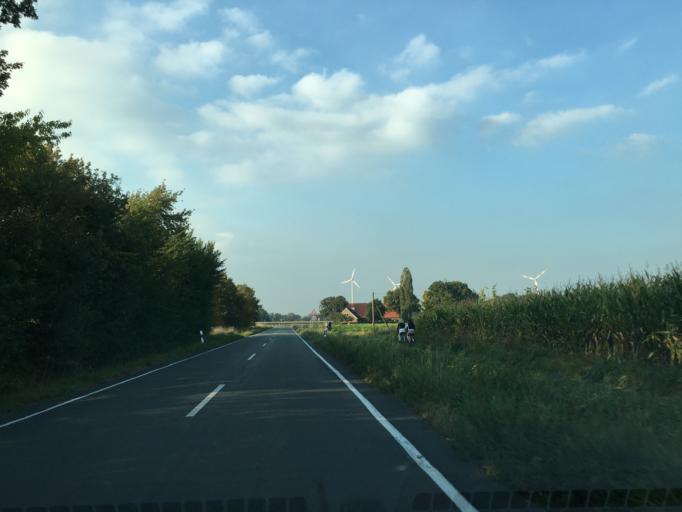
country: DE
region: North Rhine-Westphalia
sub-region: Regierungsbezirk Munster
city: Greven
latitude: 52.0299
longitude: 7.5599
